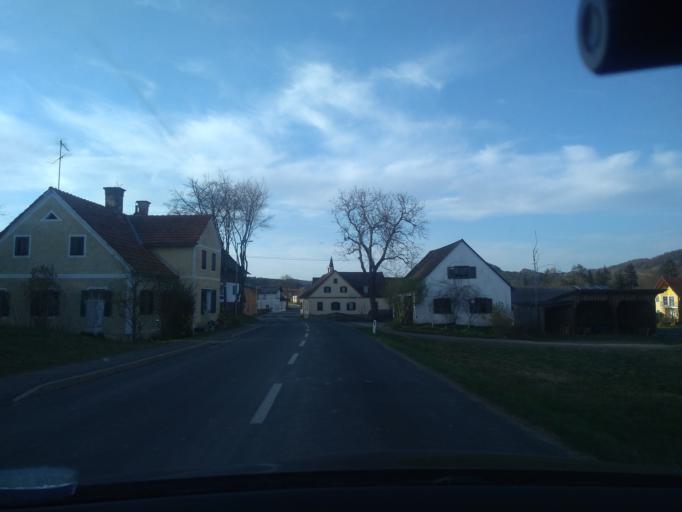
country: AT
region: Styria
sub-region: Politischer Bezirk Suedoststeiermark
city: Sankt Peter am Ottersbach
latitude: 46.8235
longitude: 15.7564
